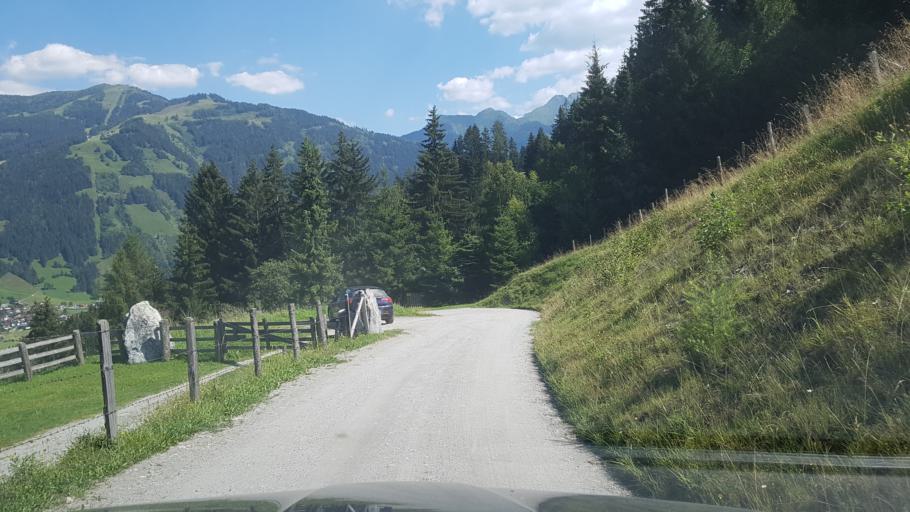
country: AT
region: Salzburg
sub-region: Politischer Bezirk Sankt Johann im Pongau
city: Dorfgastein
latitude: 47.2502
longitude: 13.0828
